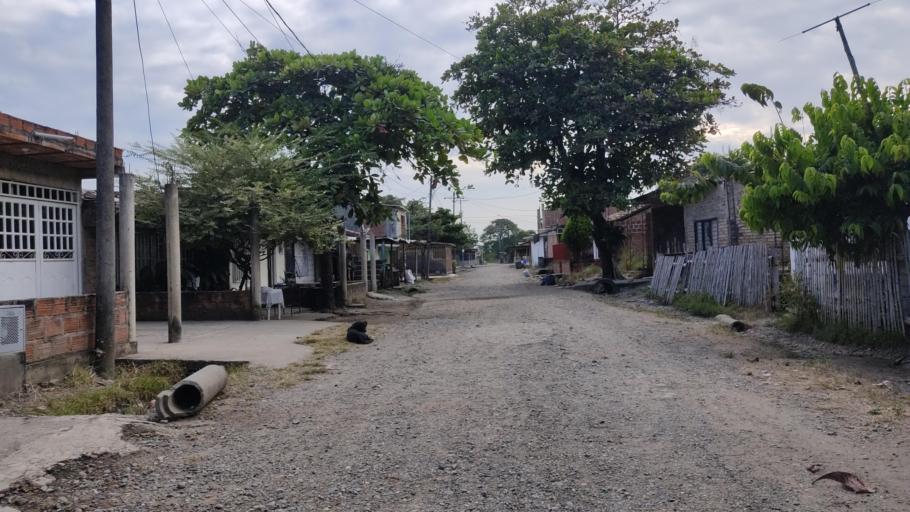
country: CO
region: Valle del Cauca
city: Jamundi
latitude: 3.1287
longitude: -76.5582
